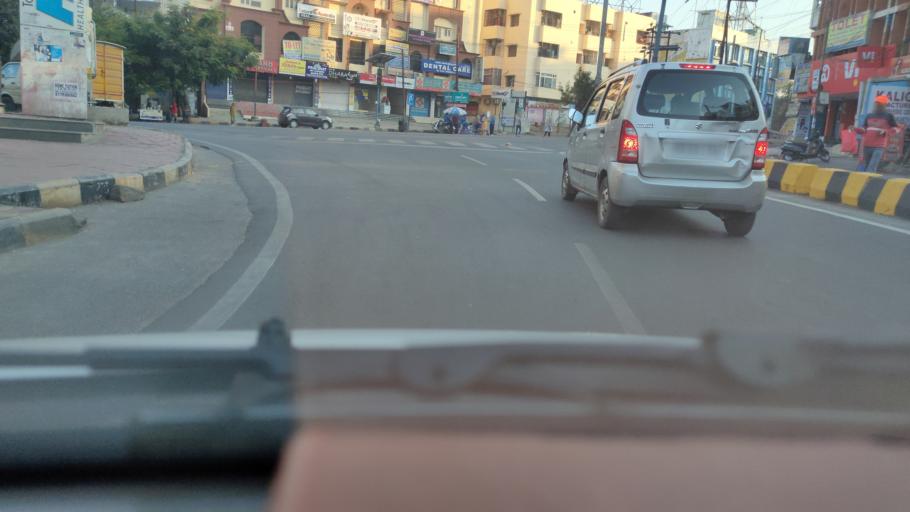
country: IN
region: Telangana
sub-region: Rangareddi
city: Gaddi Annaram
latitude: 17.4049
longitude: 78.5153
